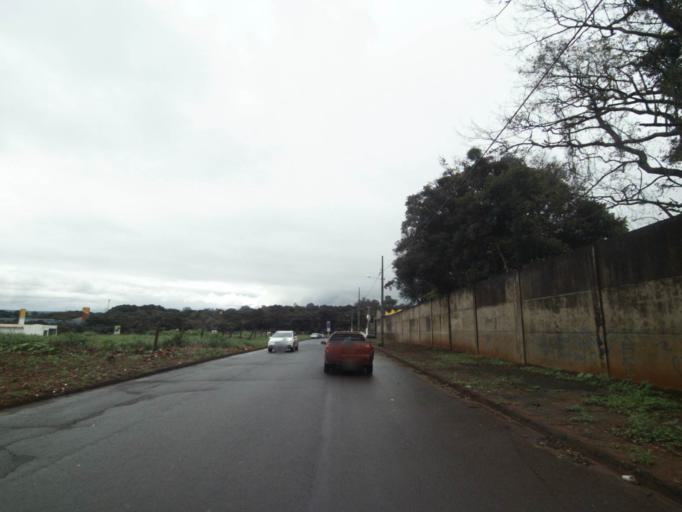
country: PY
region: Alto Parana
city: Ciudad del Este
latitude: -25.5104
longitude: -54.5804
